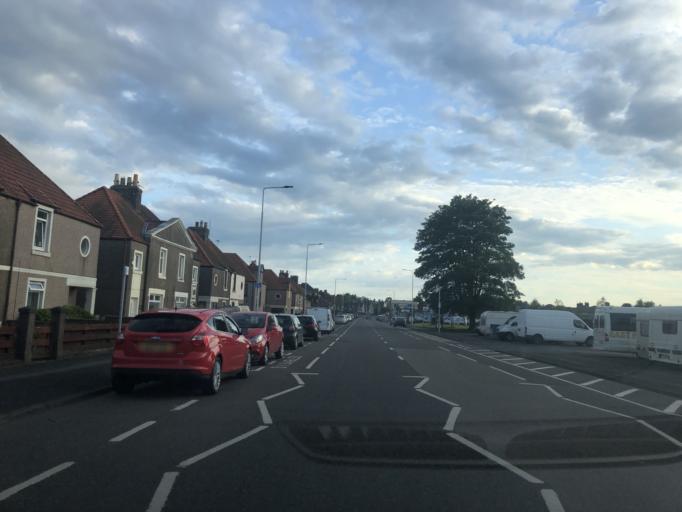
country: GB
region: Scotland
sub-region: Fife
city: Buckhaven
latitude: 56.1762
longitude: -3.0278
